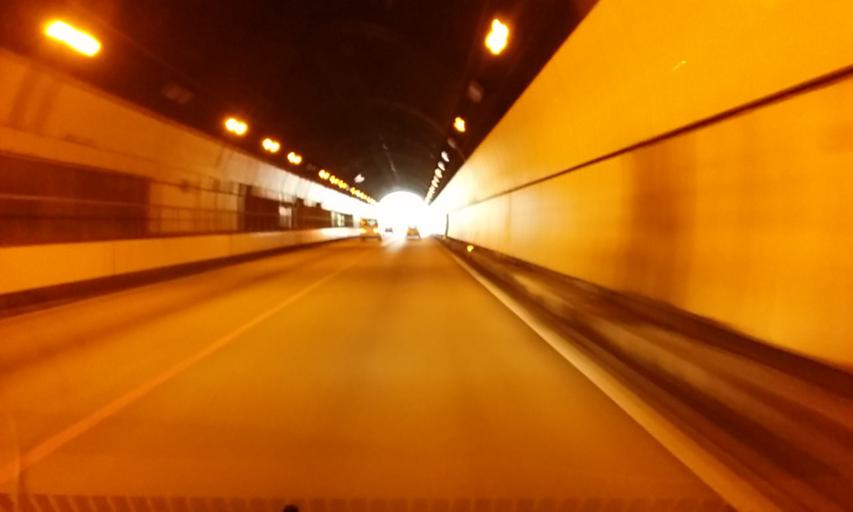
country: JP
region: Hyogo
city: Sasayama
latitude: 35.1176
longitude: 135.1652
